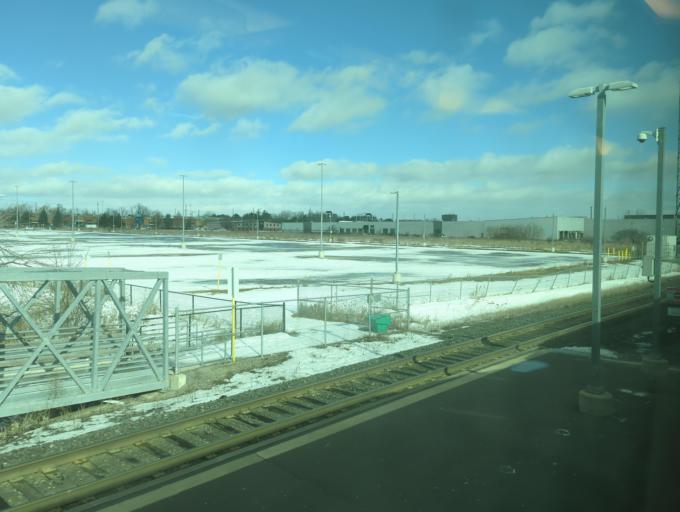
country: CA
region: Ontario
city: Burlington
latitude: 43.3803
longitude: -79.7603
